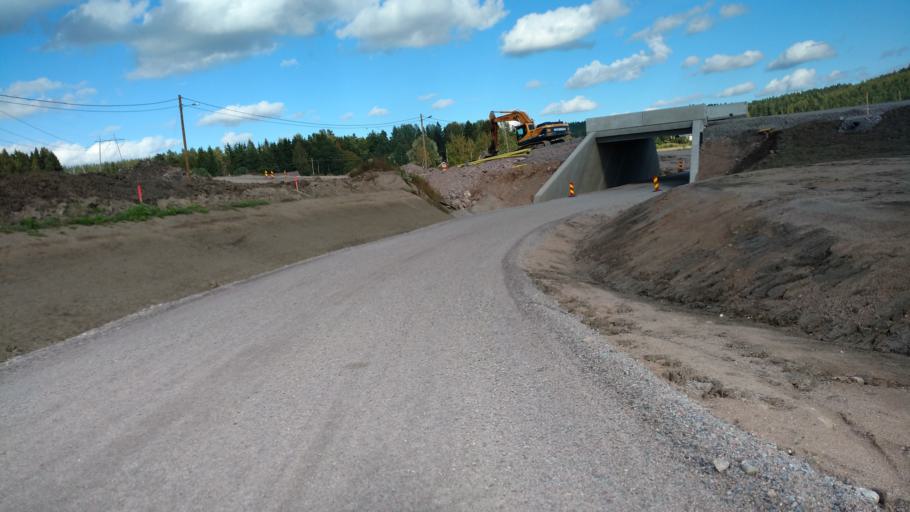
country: FI
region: Varsinais-Suomi
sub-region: Salo
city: Salo
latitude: 60.3781
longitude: 23.1742
